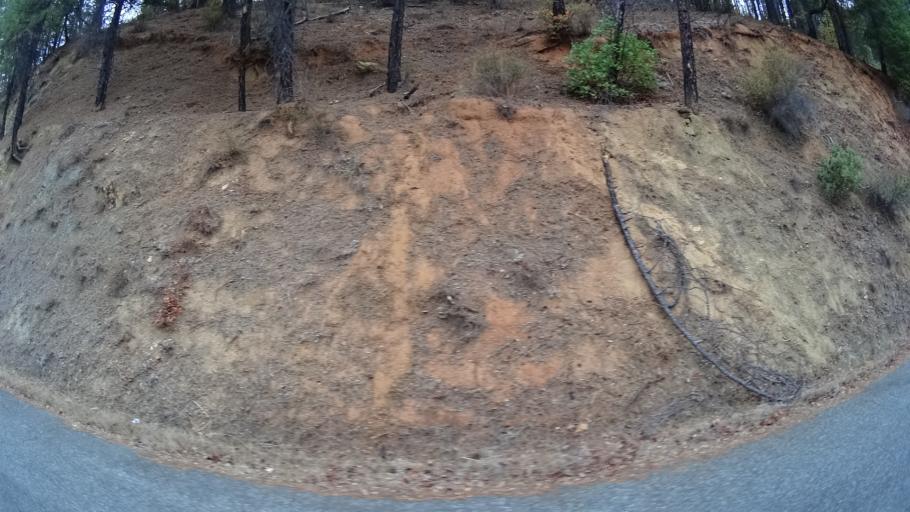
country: US
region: California
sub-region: Siskiyou County
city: Happy Camp
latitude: 41.7699
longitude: -123.3714
